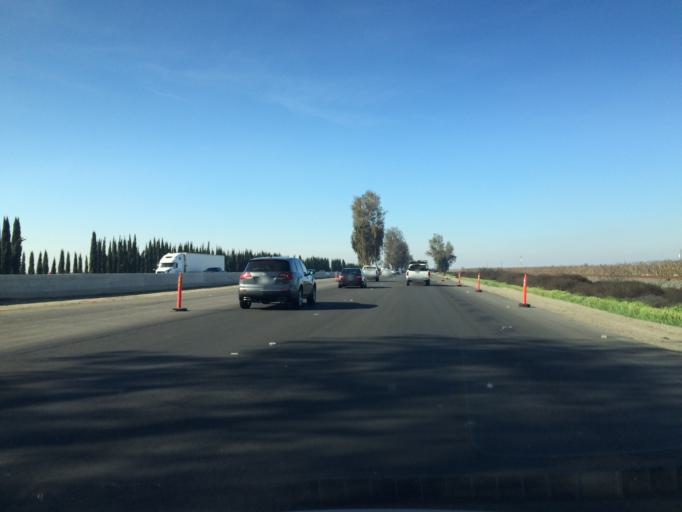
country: US
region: California
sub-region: Tulare County
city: London
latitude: 36.4632
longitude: -119.4950
